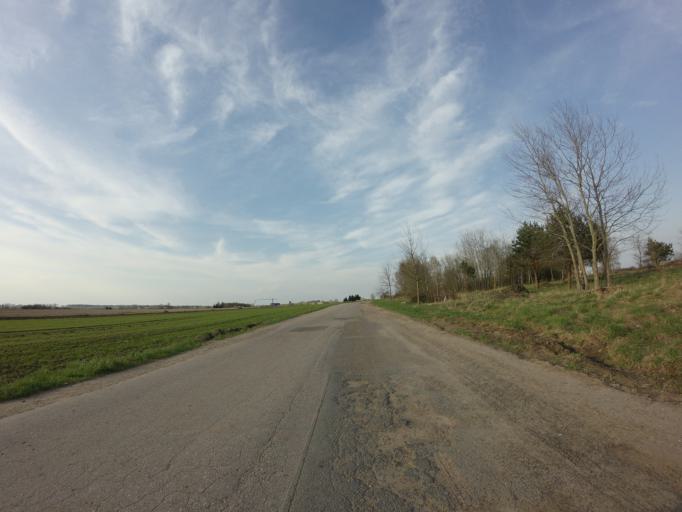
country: PL
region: West Pomeranian Voivodeship
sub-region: Powiat choszczenski
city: Choszczno
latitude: 53.1685
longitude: 15.4452
